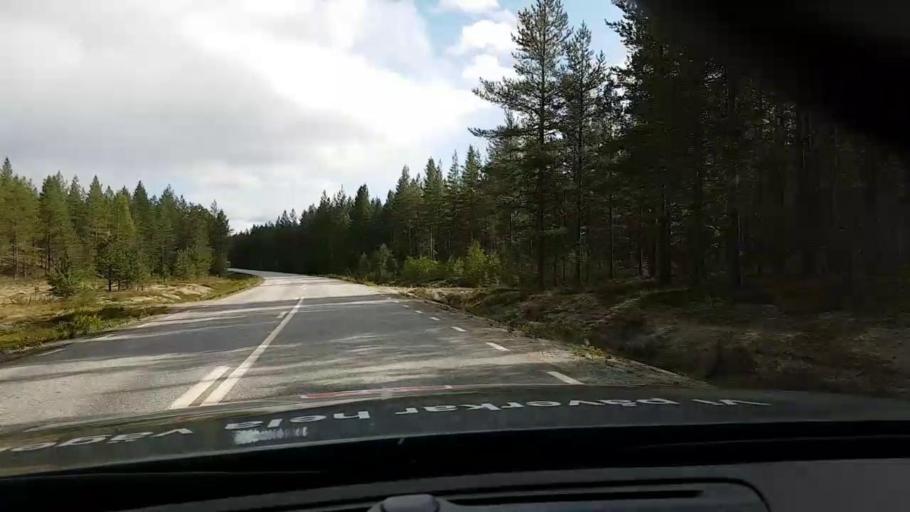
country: SE
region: Vaesternorrland
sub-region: OErnskoeldsviks Kommun
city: Bredbyn
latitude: 63.6368
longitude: 17.9036
